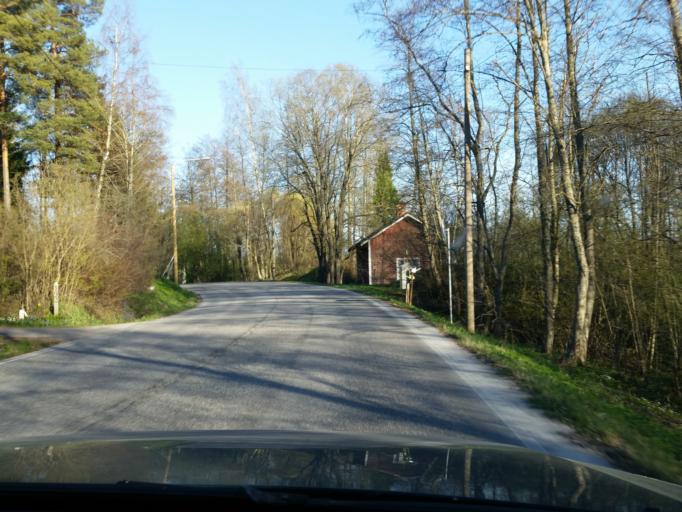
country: FI
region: Uusimaa
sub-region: Helsinki
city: Kirkkonummi
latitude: 60.1221
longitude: 24.5275
